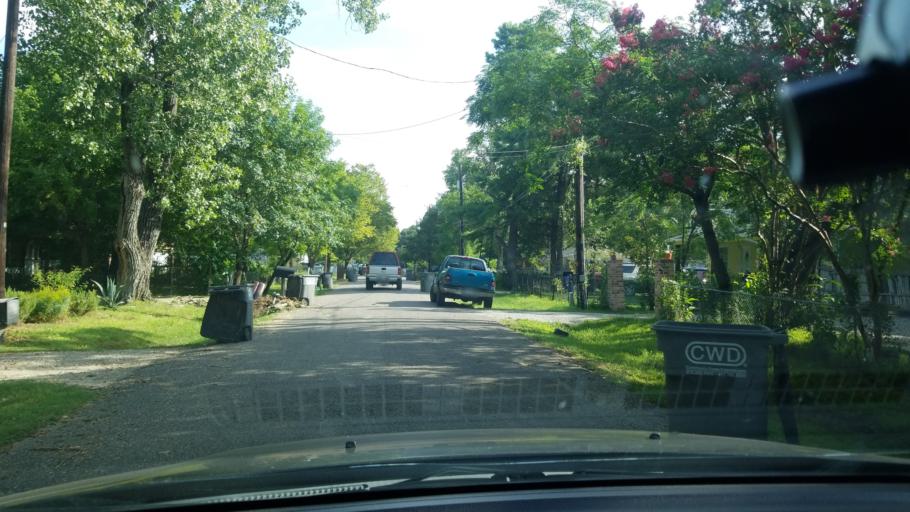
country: US
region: Texas
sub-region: Dallas County
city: Balch Springs
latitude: 32.7137
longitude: -96.6330
